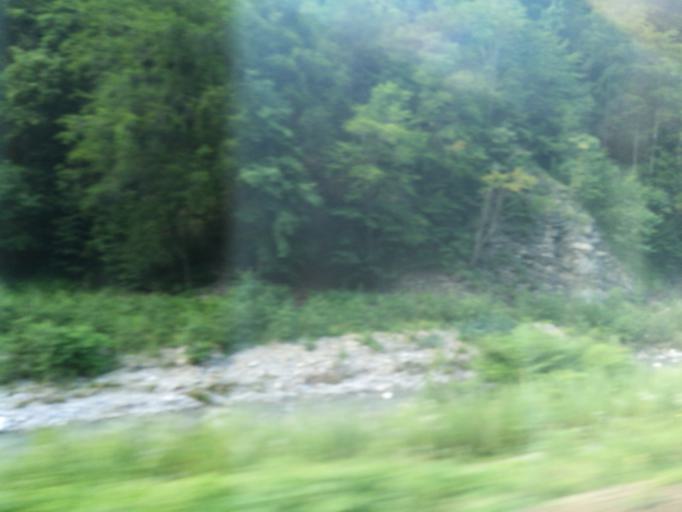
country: RO
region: Prahova
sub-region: Comuna Comarnic
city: Posada
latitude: 45.2994
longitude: 25.5857
